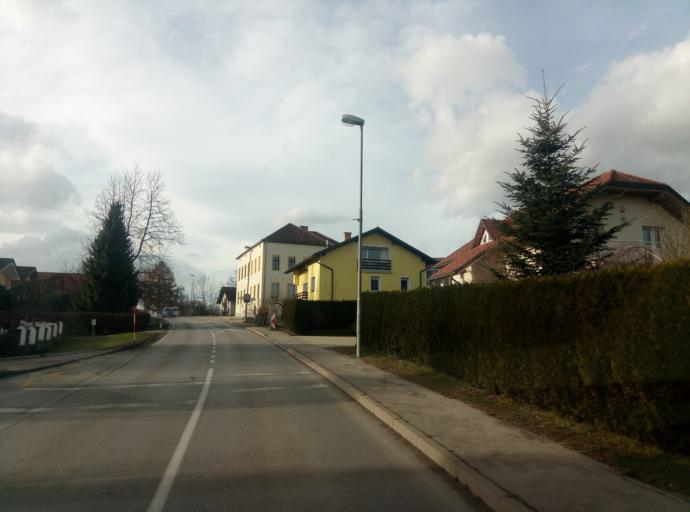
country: SI
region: Celje
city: Ljubecna
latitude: 46.2391
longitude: 15.3497
